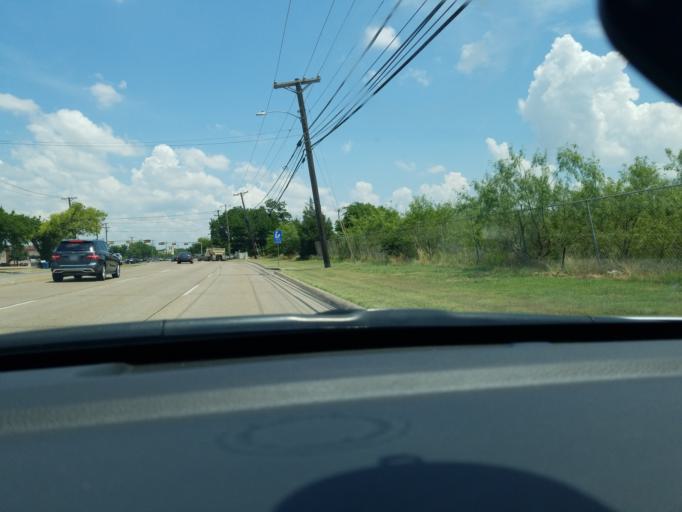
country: US
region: Texas
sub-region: Dallas County
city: Sunnyvale
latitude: 32.8126
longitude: -96.5957
